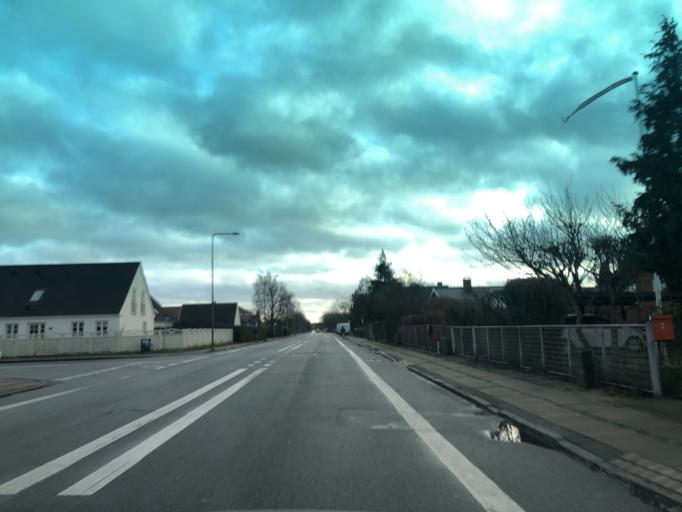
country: DK
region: Capital Region
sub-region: Tarnby Kommune
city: Tarnby
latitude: 55.6406
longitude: 12.6076
